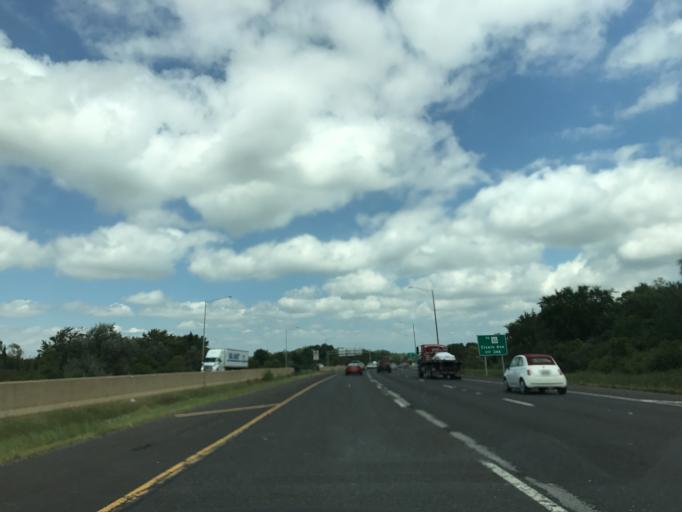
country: US
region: Illinois
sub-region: Cook County
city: Country Club Hills
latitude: 41.5770
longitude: -87.7402
